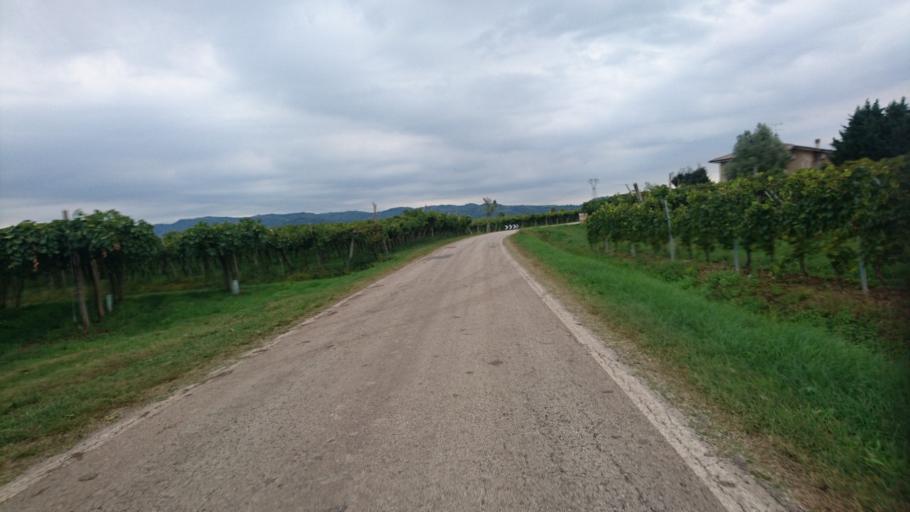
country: IT
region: Veneto
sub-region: Provincia di Verona
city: Locara
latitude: 45.4267
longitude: 11.3148
